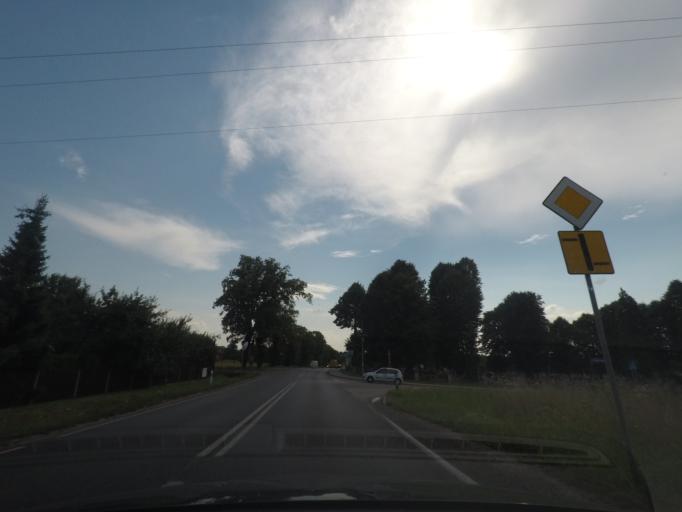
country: PL
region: Lesser Poland Voivodeship
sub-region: Powiat oswiecimski
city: Brzeszcze
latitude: 49.9796
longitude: 19.1507
